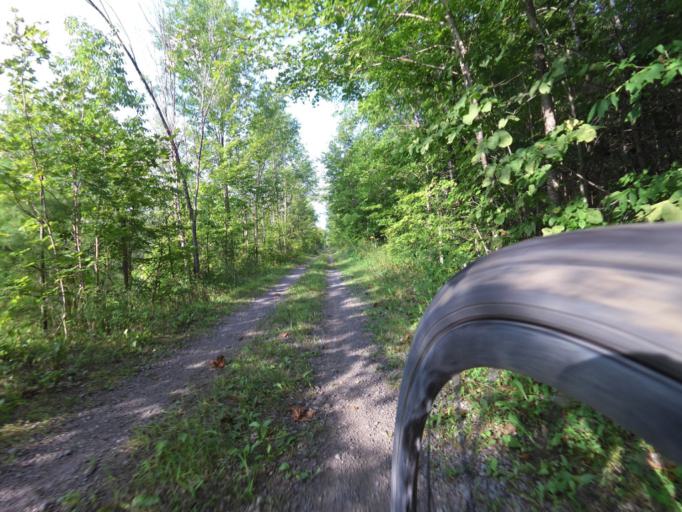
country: CA
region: Ontario
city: Kingston
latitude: 44.4755
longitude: -76.4883
